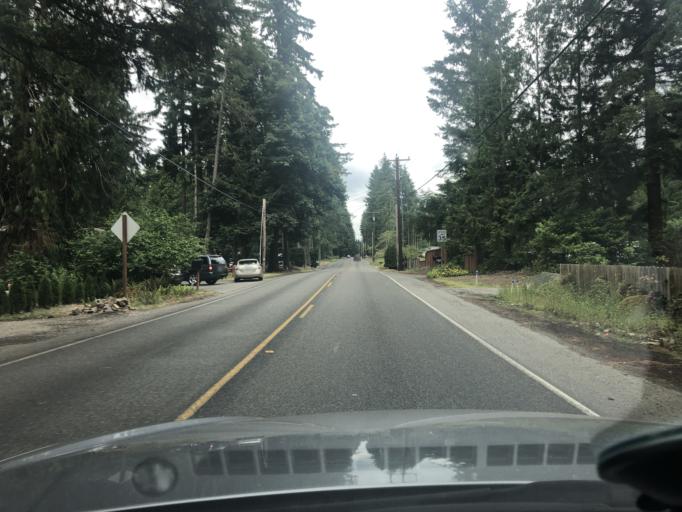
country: US
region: Washington
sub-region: King County
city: Black Diamond
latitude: 47.3354
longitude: -122.0457
